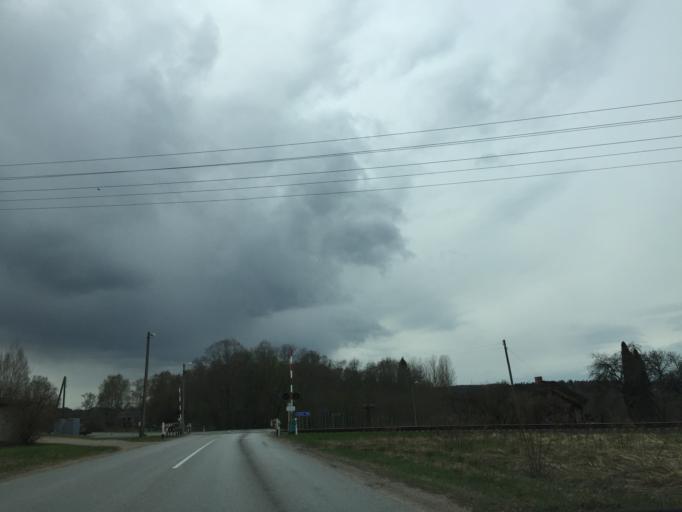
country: LV
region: Priekuli
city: Priekuli
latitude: 57.3445
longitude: 25.3408
